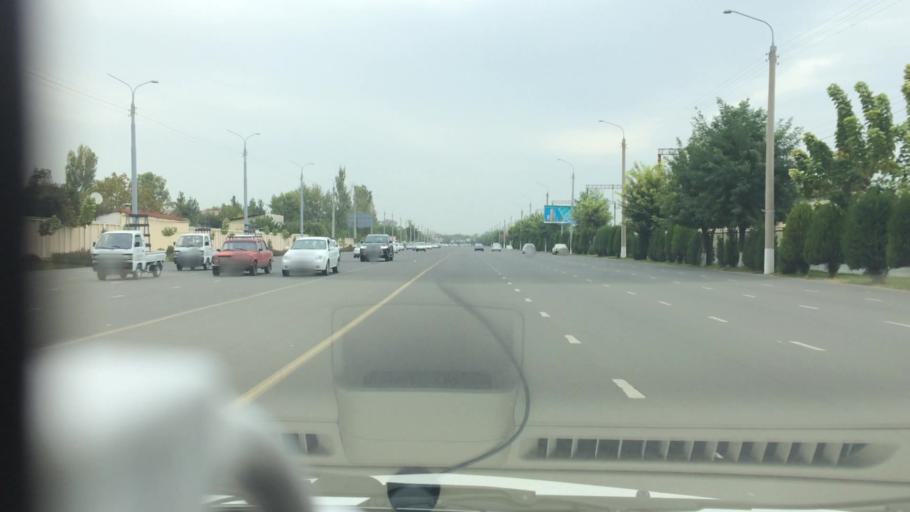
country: UZ
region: Toshkent Shahri
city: Tashkent
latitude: 41.2800
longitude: 69.2745
